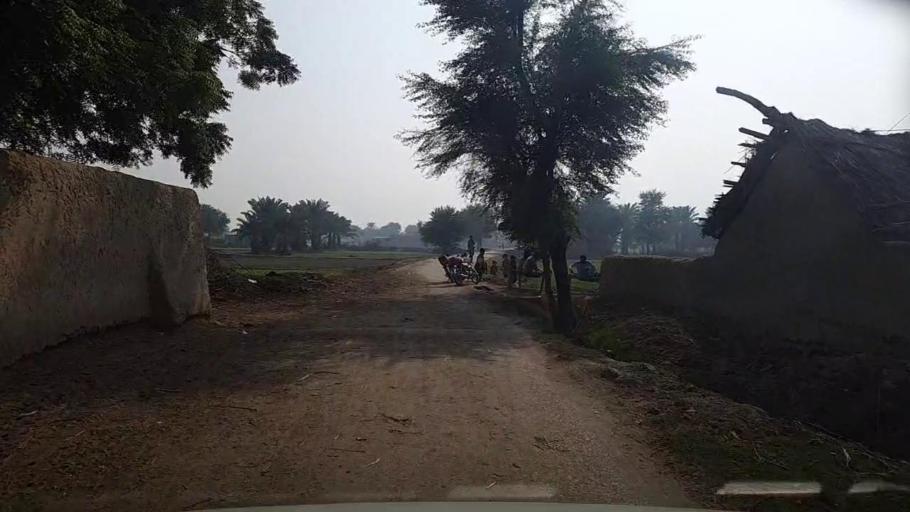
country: PK
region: Sindh
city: Setharja Old
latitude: 27.1203
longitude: 68.5161
